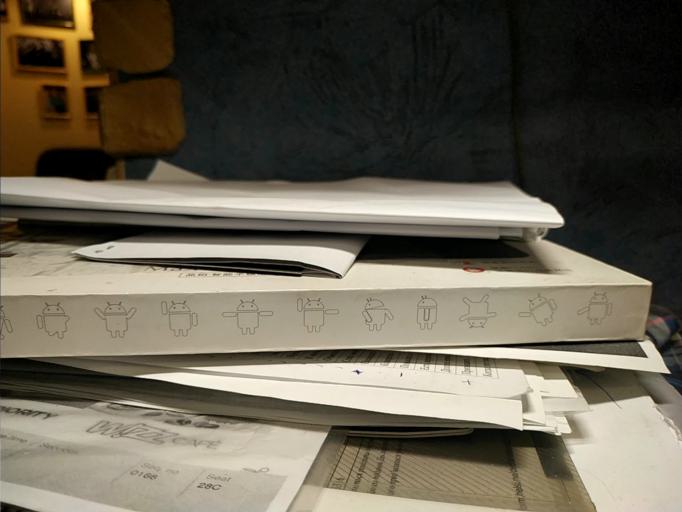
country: RU
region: Tverskaya
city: Zubtsov
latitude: 56.0826
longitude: 34.7884
